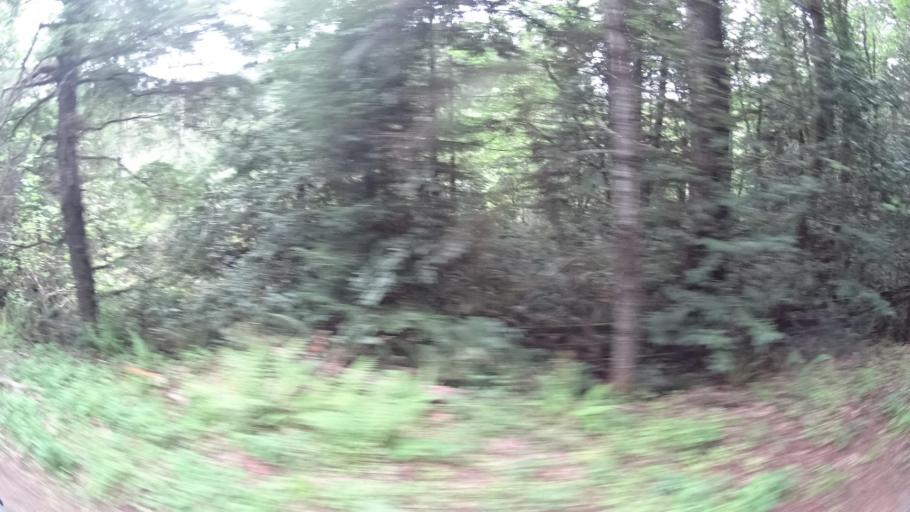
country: US
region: California
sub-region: Humboldt County
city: Blue Lake
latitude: 40.9609
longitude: -123.8384
